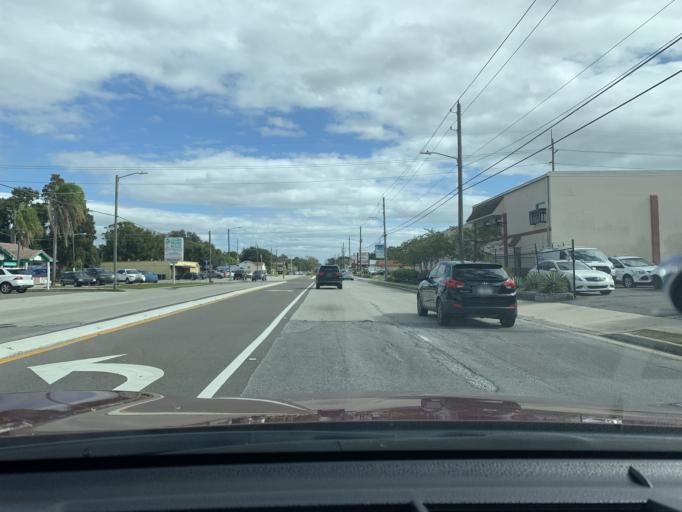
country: US
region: Florida
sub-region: Hillsborough County
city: Tampa
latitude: 27.9667
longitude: -82.5002
